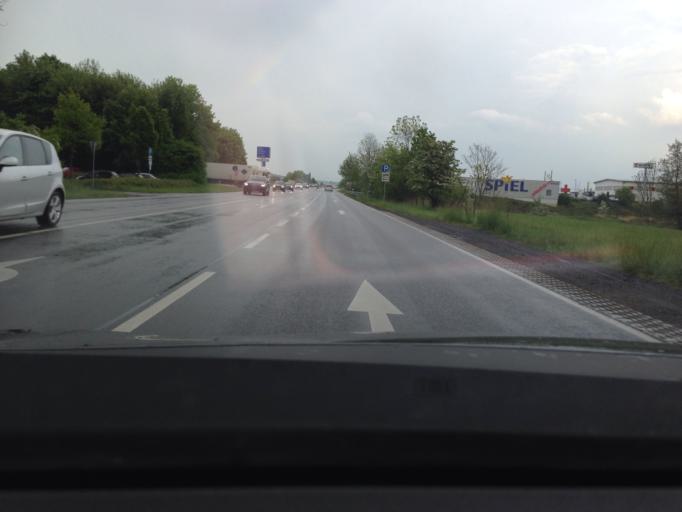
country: DE
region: Hesse
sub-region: Regierungsbezirk Giessen
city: Reiskirchen
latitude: 50.5956
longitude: 8.8145
